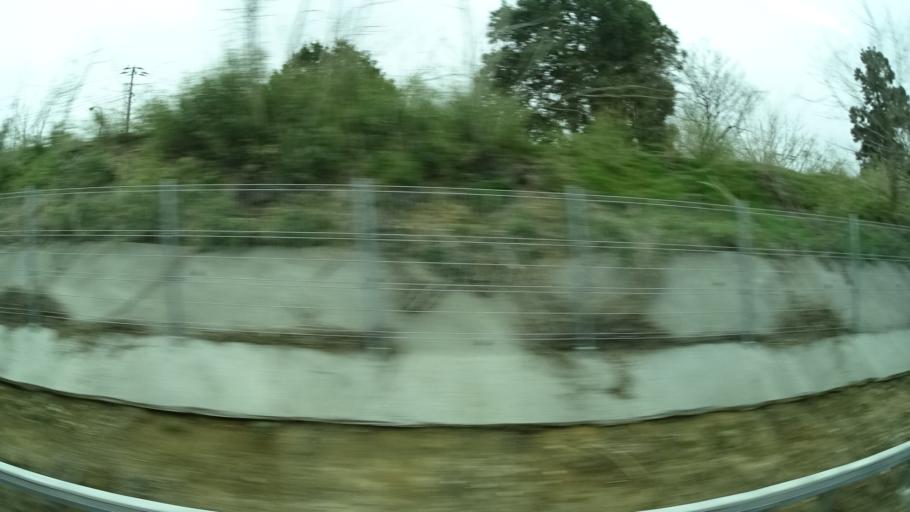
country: JP
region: Fukushima
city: Namie
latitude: 37.4024
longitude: 140.9854
